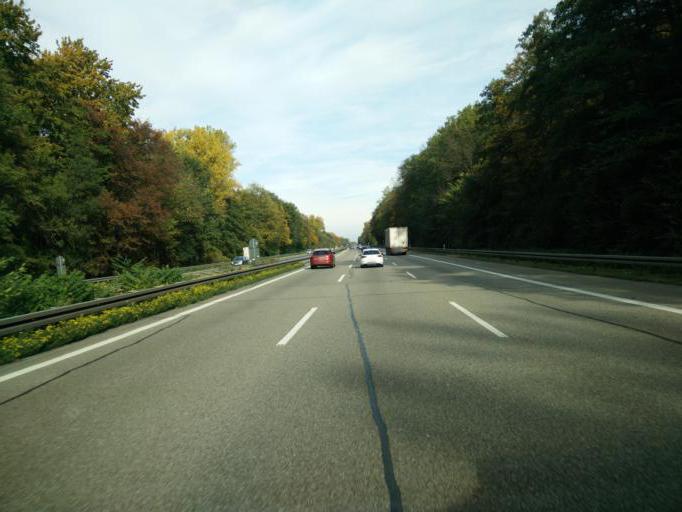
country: DE
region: Baden-Wuerttemberg
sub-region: Karlsruhe Region
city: Weingarten
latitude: 49.0310
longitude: 8.4814
